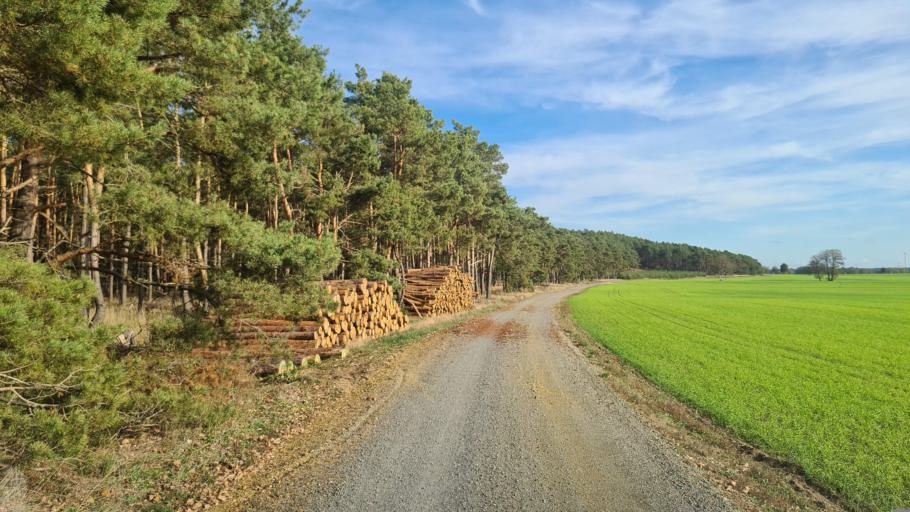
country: DE
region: Brandenburg
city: Schlieben
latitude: 51.7378
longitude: 13.4106
